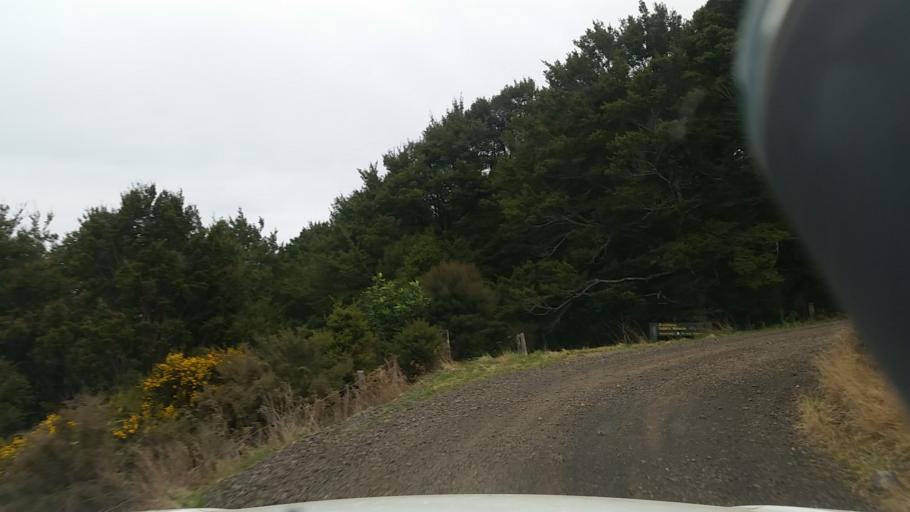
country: NZ
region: Canterbury
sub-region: Christchurch City
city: Christchurch
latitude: -43.8365
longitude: 173.0026
